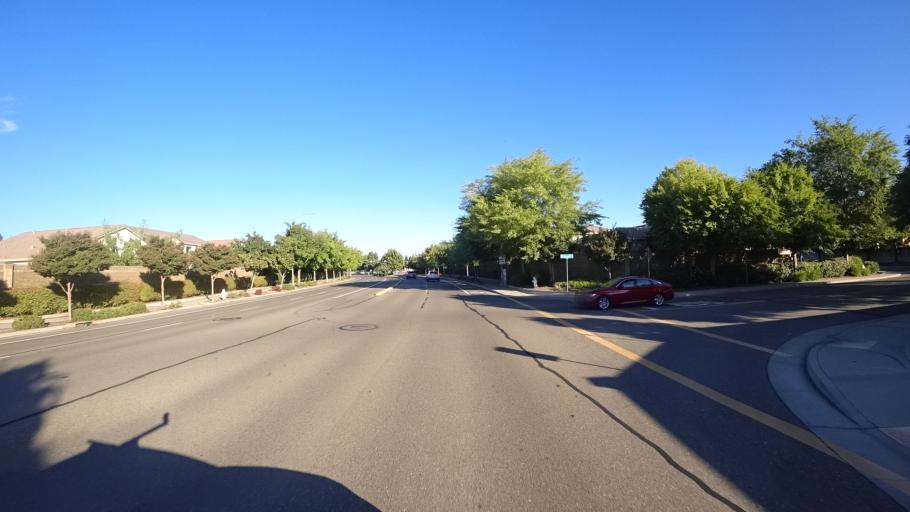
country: US
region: California
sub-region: Sacramento County
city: Laguna
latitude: 38.4461
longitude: -121.3926
